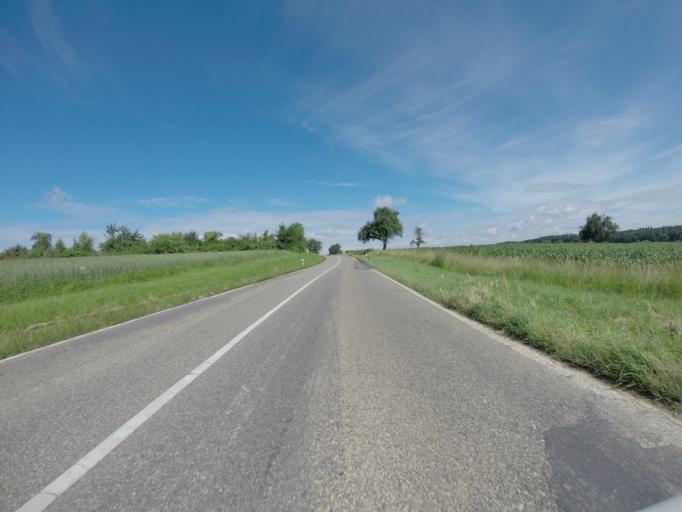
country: DE
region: Baden-Wuerttemberg
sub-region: Karlsruhe Region
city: Ettlingen
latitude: 48.9299
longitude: 8.4990
